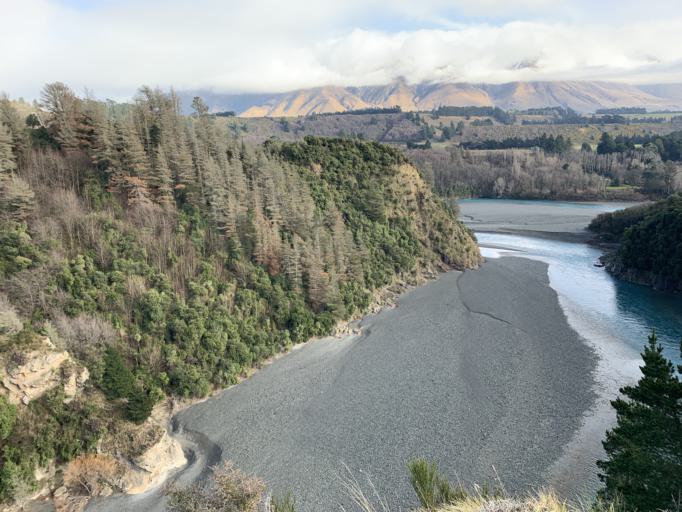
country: NZ
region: Canterbury
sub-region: Ashburton District
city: Methven
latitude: -43.5149
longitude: 171.6466
